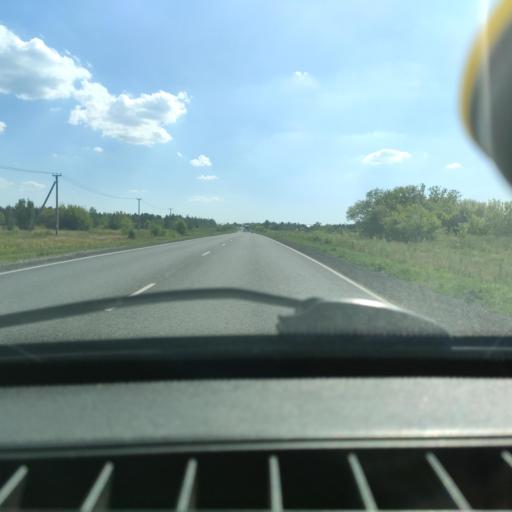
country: RU
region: Samara
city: Povolzhskiy
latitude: 53.6879
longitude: 49.7287
